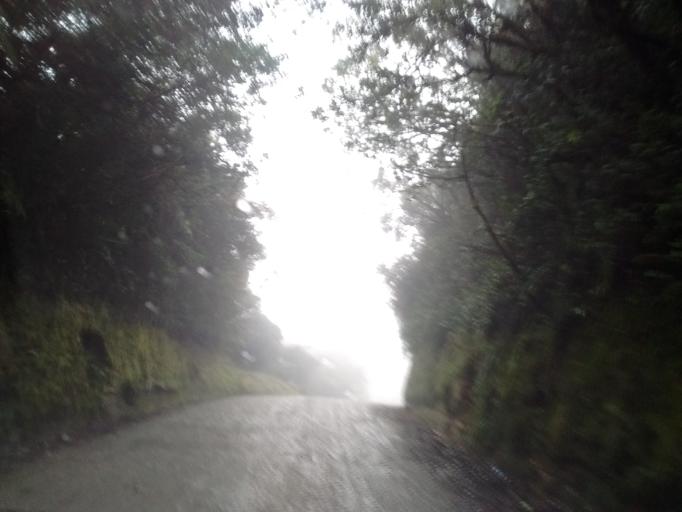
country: CO
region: Cauca
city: Paispamba
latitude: 2.1531
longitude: -76.4186
